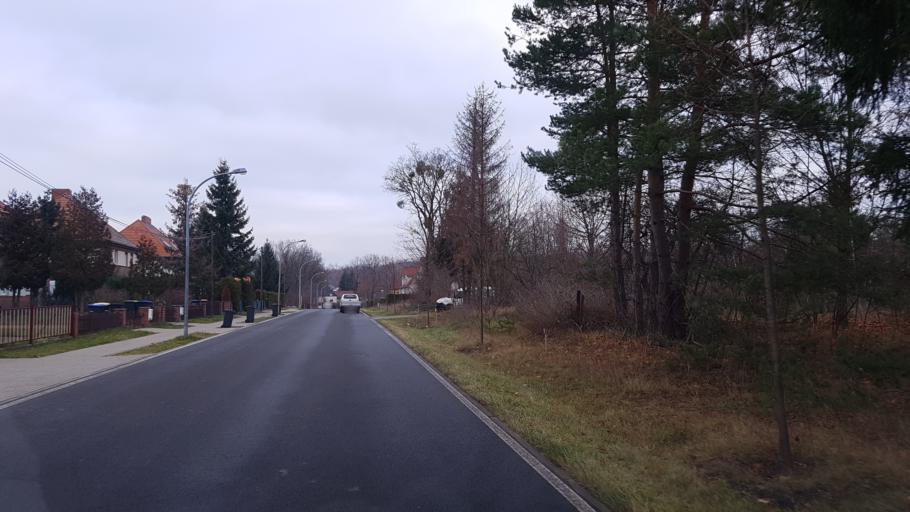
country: DE
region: Brandenburg
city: Sallgast
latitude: 51.5617
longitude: 13.8692
